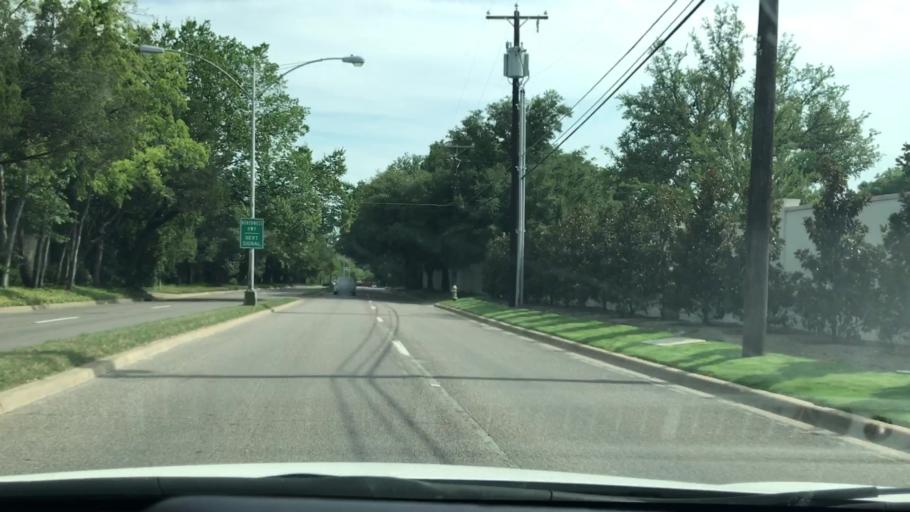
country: US
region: Texas
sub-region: Dallas County
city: University Park
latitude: 32.8703
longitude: -96.8214
